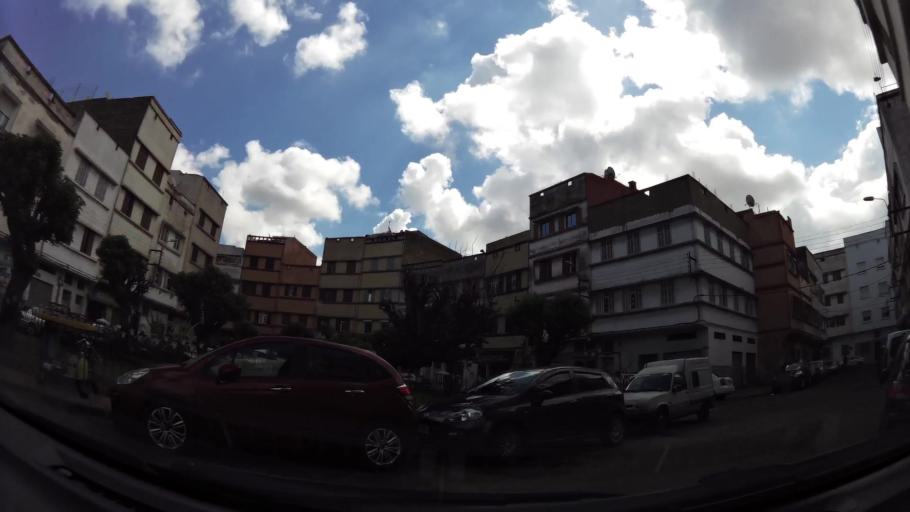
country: MA
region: Grand Casablanca
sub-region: Casablanca
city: Casablanca
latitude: 33.5609
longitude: -7.6060
